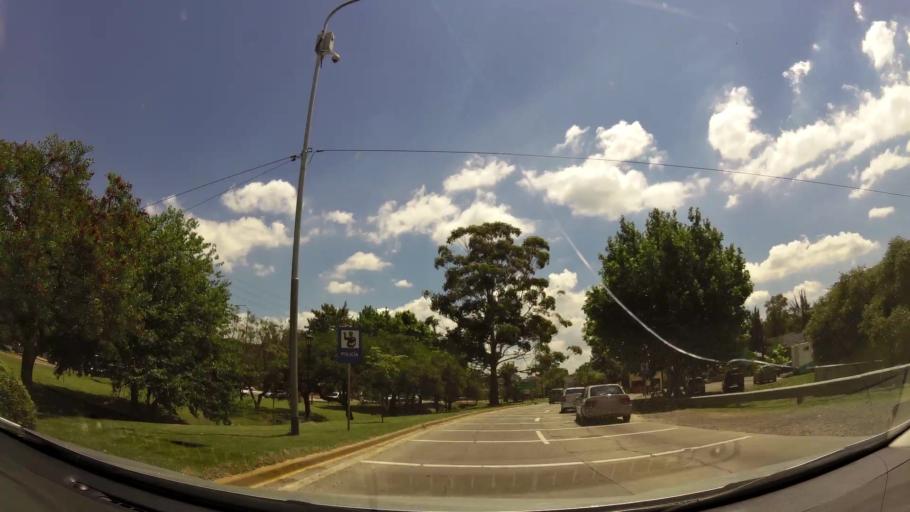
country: AR
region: Buenos Aires
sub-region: Partido de Tigre
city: Tigre
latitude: -34.4299
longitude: -58.5917
